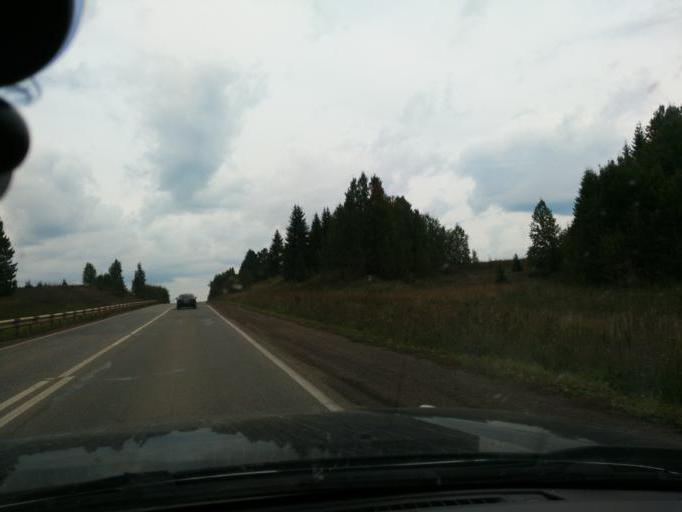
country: RU
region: Perm
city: Chernushka
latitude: 56.7095
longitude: 56.1821
